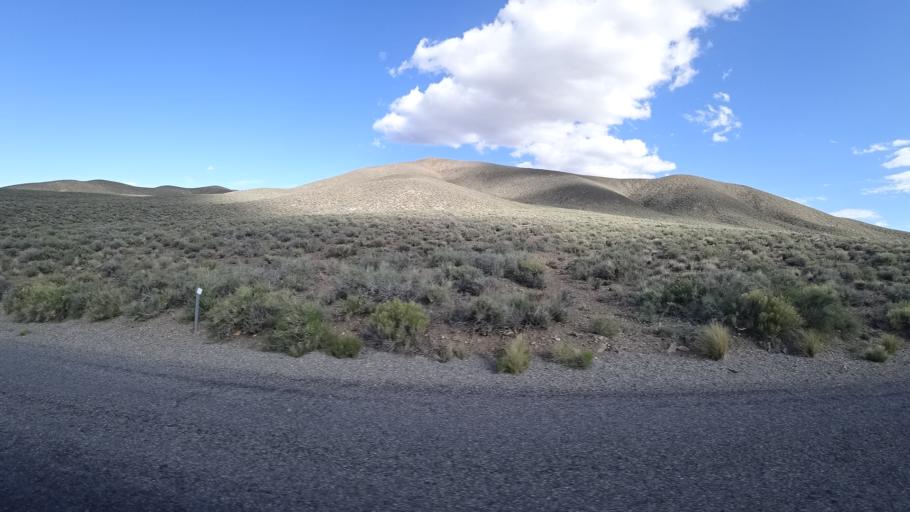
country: US
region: California
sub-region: San Bernardino County
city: Searles Valley
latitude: 36.3276
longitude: -117.1485
